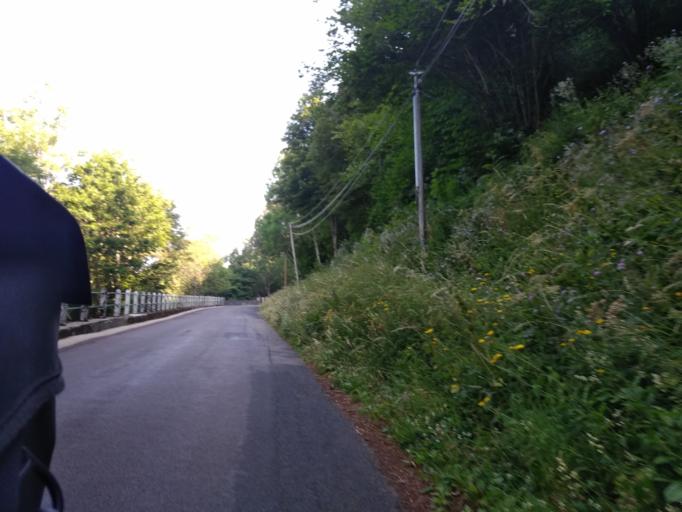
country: FR
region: Auvergne
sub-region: Departement du Puy-de-Dome
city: Mont-Dore
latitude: 45.5739
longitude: 2.8141
